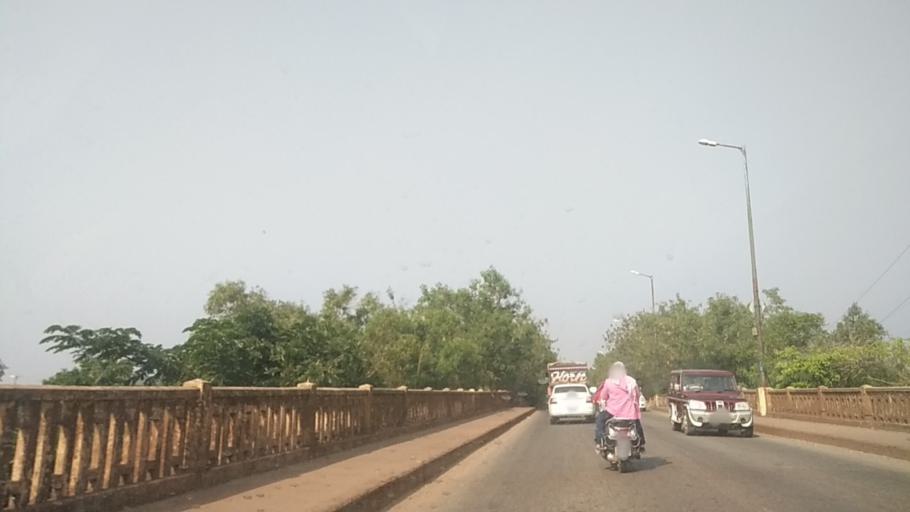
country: IN
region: Goa
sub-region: North Goa
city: Colovale
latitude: 15.6499
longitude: 73.8367
